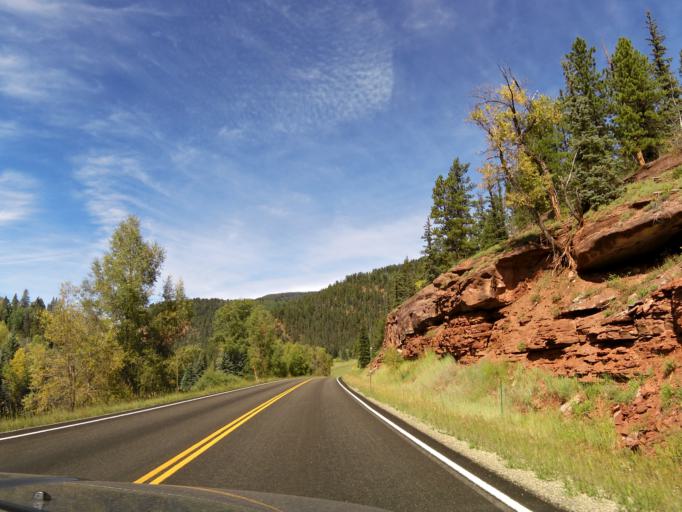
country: US
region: Colorado
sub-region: Montezuma County
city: Mancos
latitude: 37.5924
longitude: -108.1282
